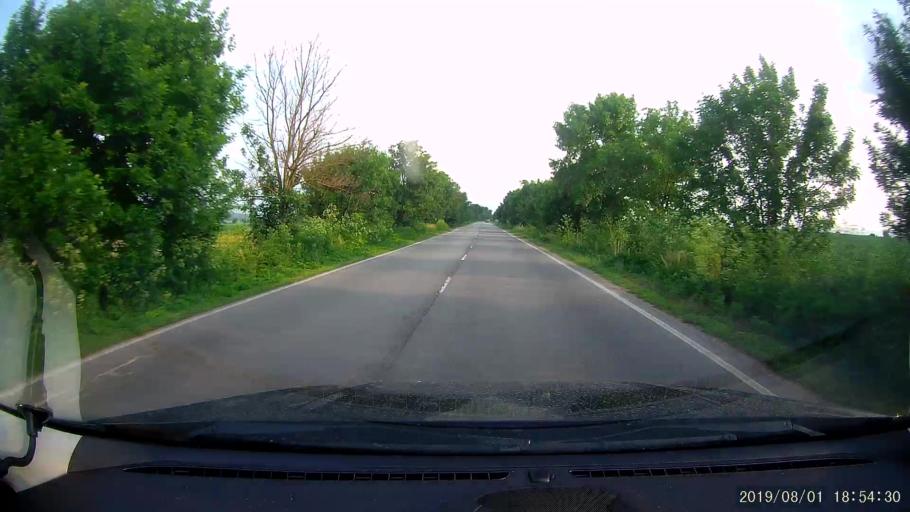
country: BG
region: Shumen
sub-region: Obshtina Shumen
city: Shumen
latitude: 43.1969
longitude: 27.0021
